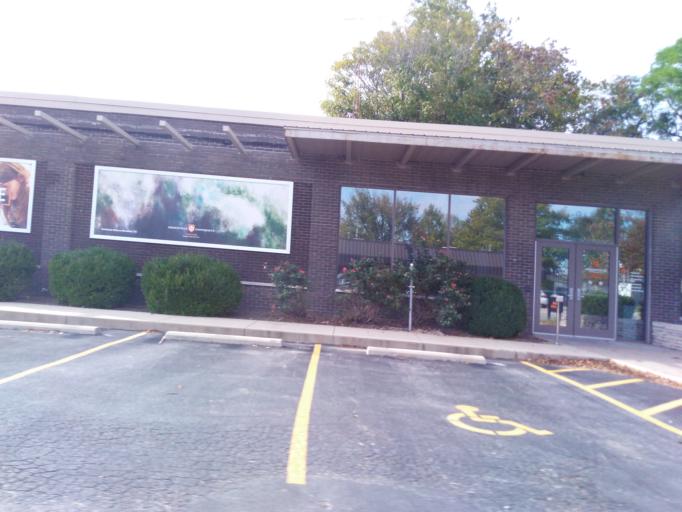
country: US
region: Illinois
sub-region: Bond County
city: Greenville
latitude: 38.8940
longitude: -89.4121
